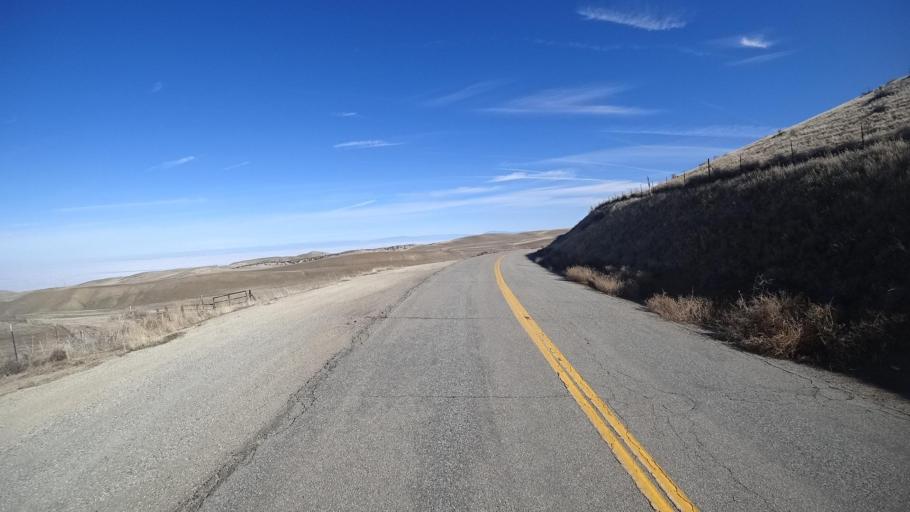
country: US
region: California
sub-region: Kern County
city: Maricopa
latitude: 34.9348
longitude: -119.4110
